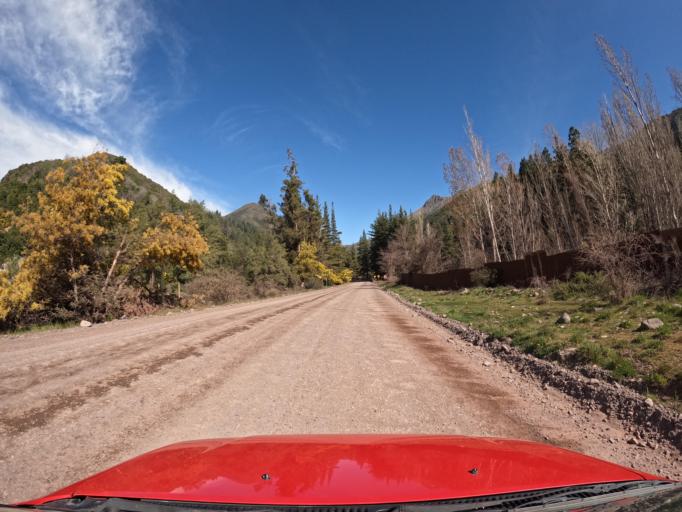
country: CL
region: O'Higgins
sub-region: Provincia de Colchagua
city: Chimbarongo
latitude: -35.0108
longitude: -70.7470
